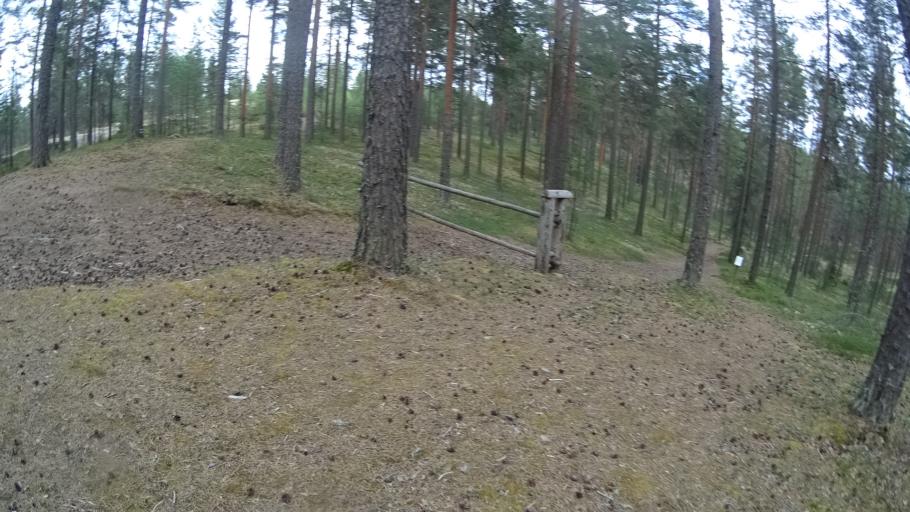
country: FI
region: Satakunta
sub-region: Pohjois-Satakunta
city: Jaemijaervi
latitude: 61.7702
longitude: 22.7872
